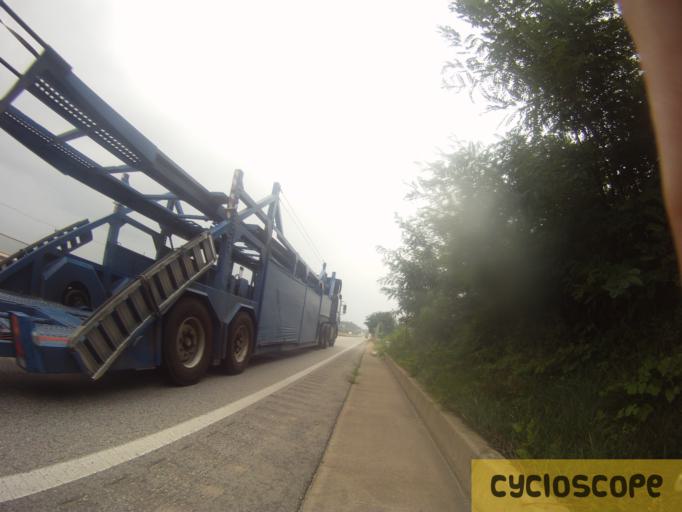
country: KR
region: Gyeonggi-do
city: Hwaseong-si
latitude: 37.1409
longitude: 126.8659
